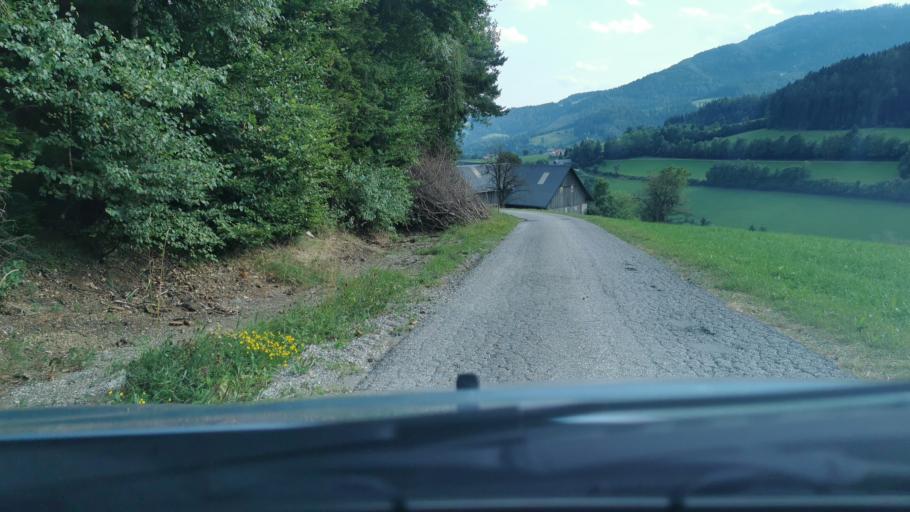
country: AT
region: Styria
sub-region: Politischer Bezirk Weiz
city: Koglhof
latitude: 47.3188
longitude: 15.6711
